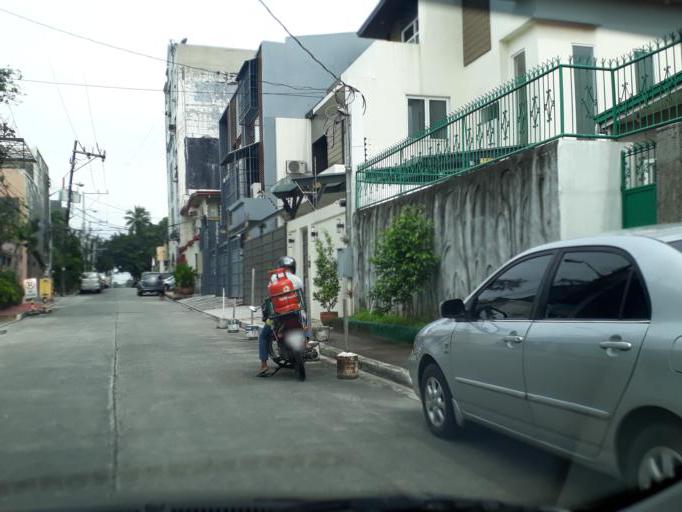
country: PH
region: Metro Manila
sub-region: Quezon City
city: Quezon City
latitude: 14.6319
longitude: 121.0386
